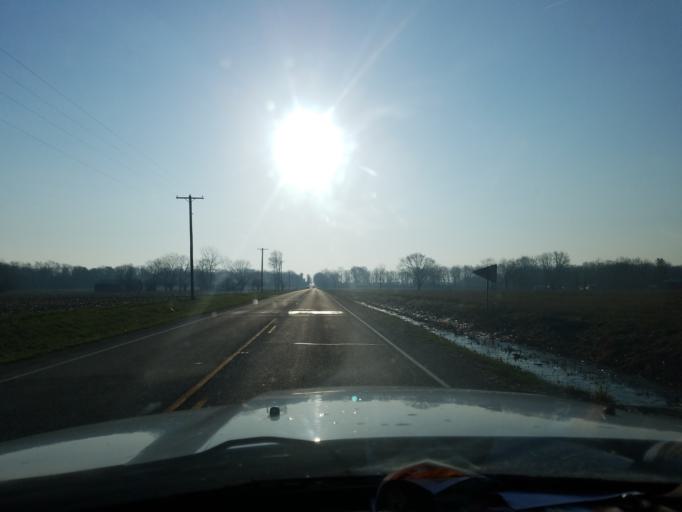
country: US
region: Indiana
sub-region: Vigo County
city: Seelyville
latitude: 39.3897
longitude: -87.2235
